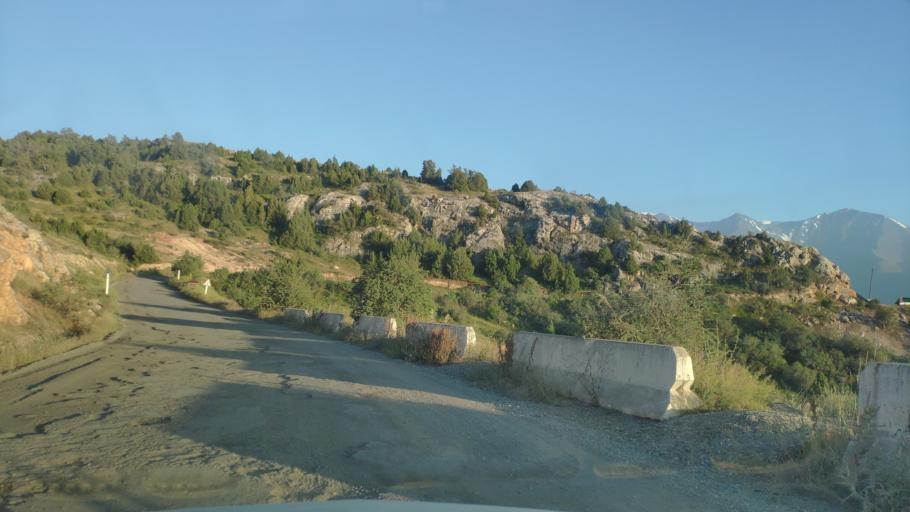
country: TJ
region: Viloyati Sughd
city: Ayni
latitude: 39.6353
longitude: 68.4624
